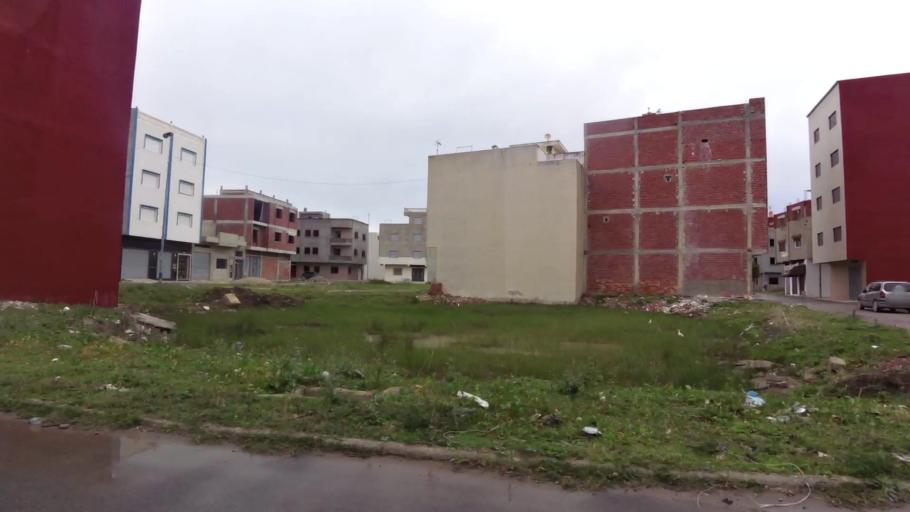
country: MA
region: Tanger-Tetouan
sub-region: Tetouan
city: Martil
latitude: 35.6138
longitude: -5.2983
